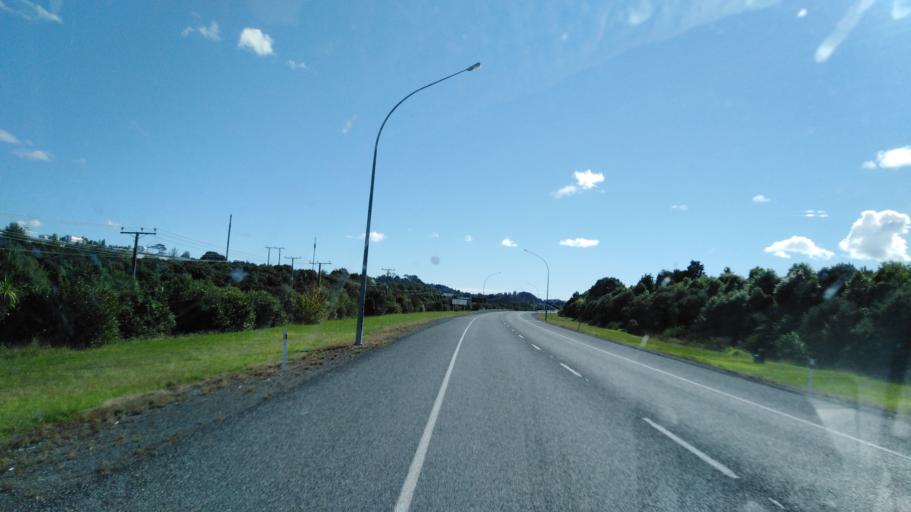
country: NZ
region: Bay of Plenty
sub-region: Tauranga City
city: Tauranga
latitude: -37.7443
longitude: 176.1045
